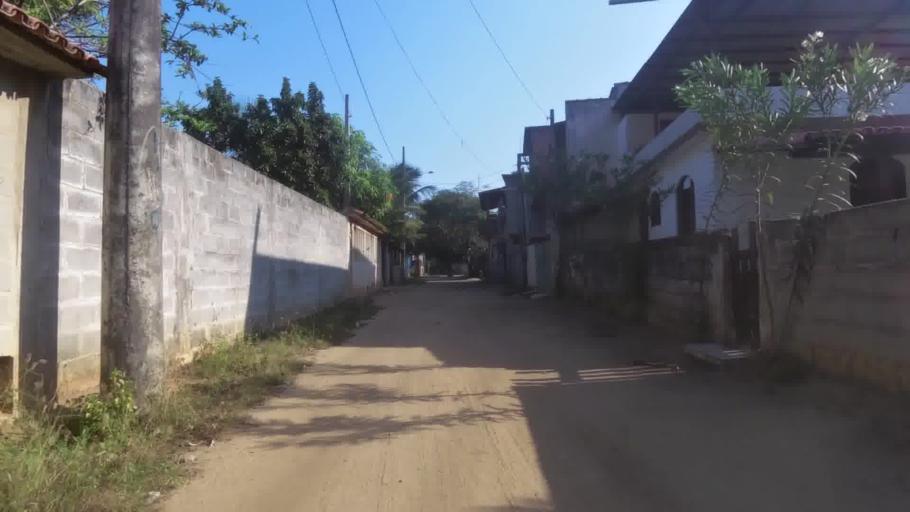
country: BR
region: Espirito Santo
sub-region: Piuma
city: Piuma
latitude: -20.8609
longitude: -40.7578
